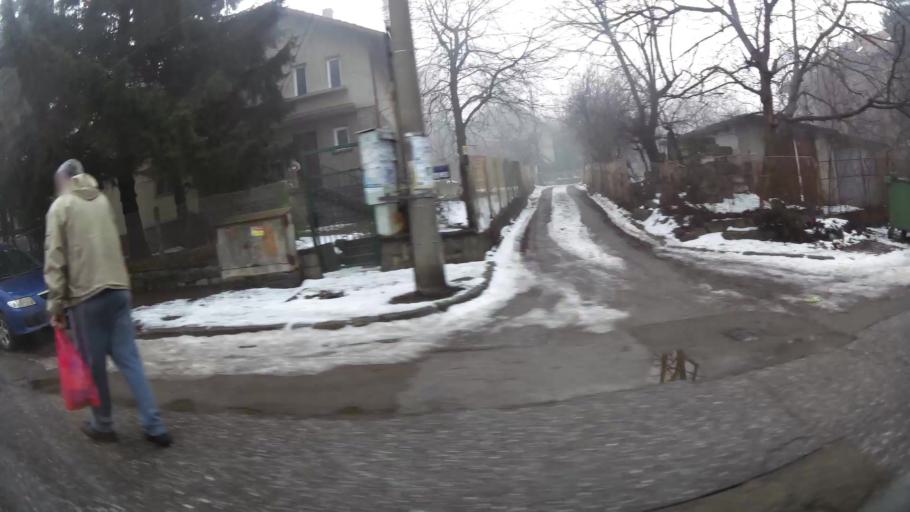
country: BG
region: Sofia-Capital
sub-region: Stolichna Obshtina
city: Sofia
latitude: 42.6591
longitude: 23.2514
